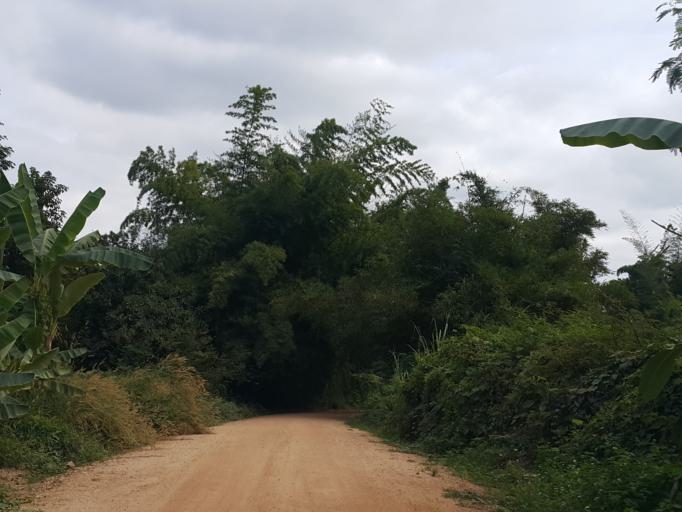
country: TH
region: Lampang
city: Hang Chat
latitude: 18.4757
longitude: 99.4123
